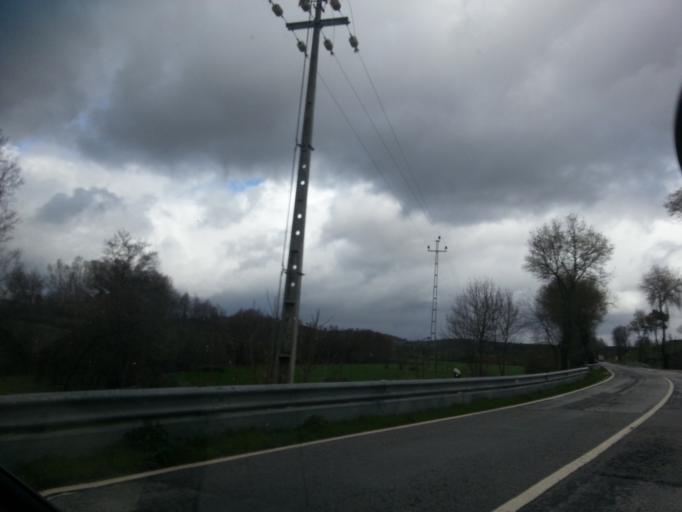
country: PT
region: Guarda
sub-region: Fornos de Algodres
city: Fornos de Algodres
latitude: 40.5690
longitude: -7.4686
